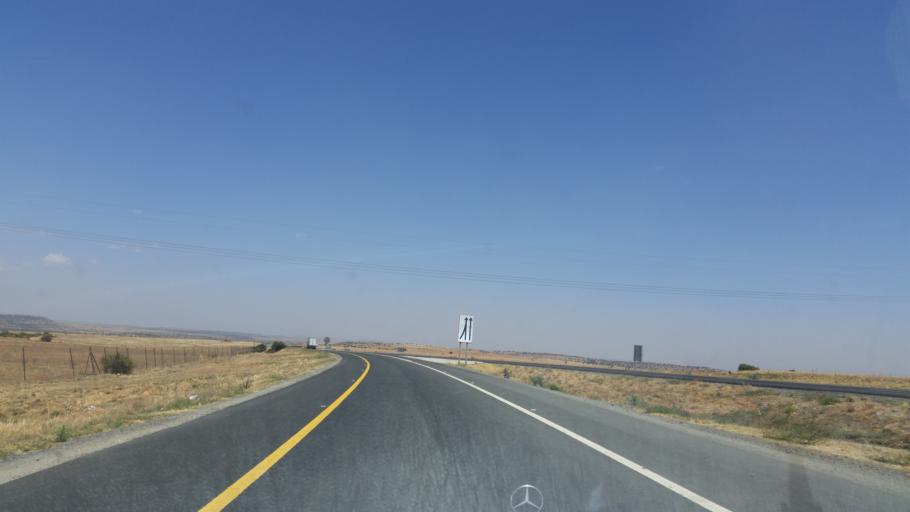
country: ZA
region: Orange Free State
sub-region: Lejweleputswa District Municipality
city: Winburg
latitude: -28.5018
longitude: 26.9967
